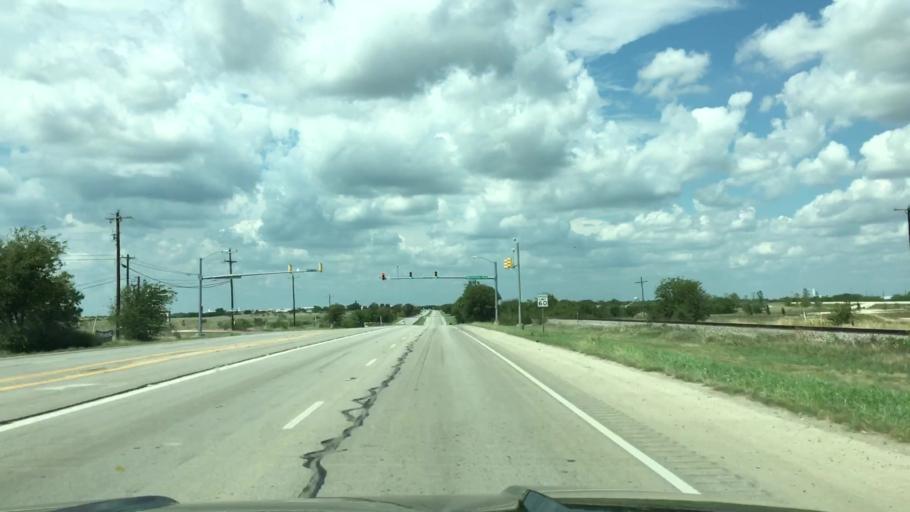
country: US
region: Texas
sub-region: Tarrant County
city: Eagle Mountain
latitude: 32.9077
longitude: -97.4037
